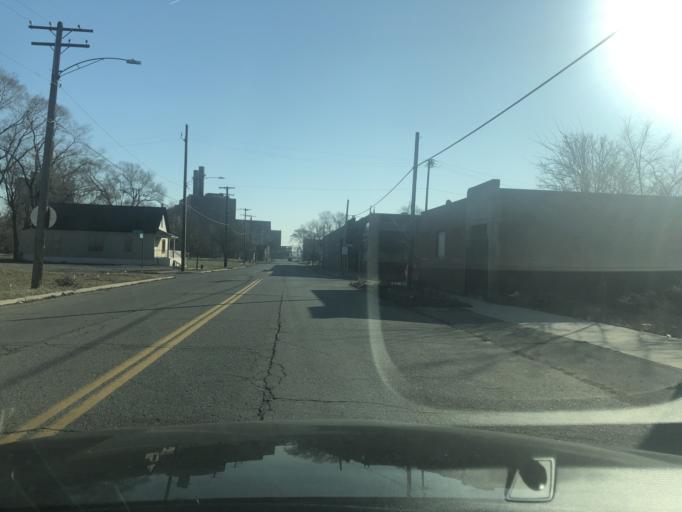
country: US
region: Michigan
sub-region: Wayne County
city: River Rouge
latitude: 42.3066
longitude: -83.0938
